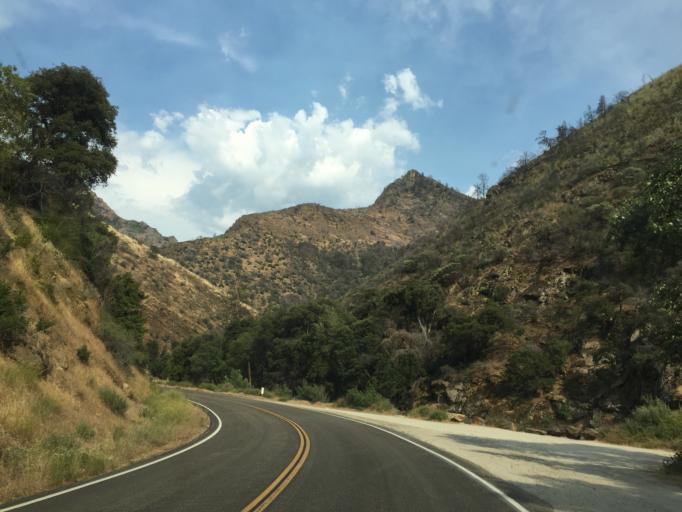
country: US
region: California
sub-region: Tulare County
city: Three Rivers
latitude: 36.8118
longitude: -118.8149
